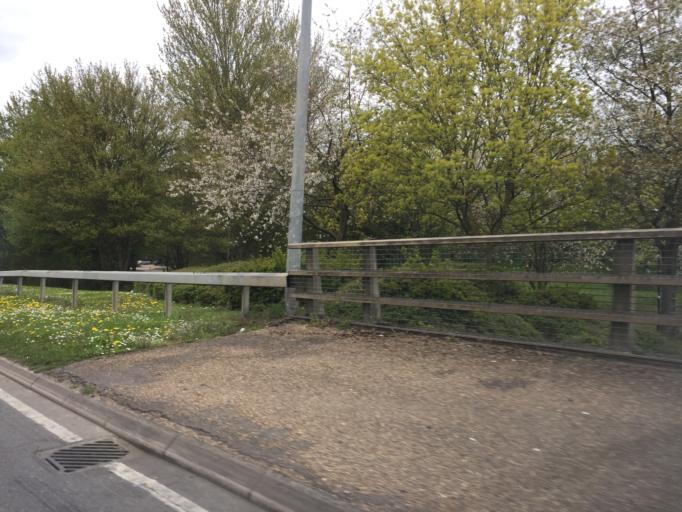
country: GB
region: England
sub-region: Milton Keynes
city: Milton Keynes
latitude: 52.0552
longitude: -0.7282
